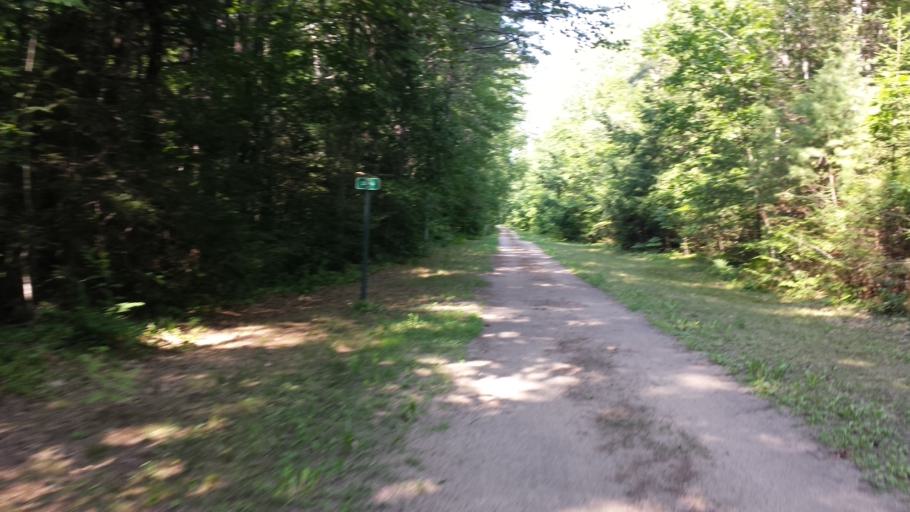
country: US
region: Maine
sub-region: York County
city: Kennebunk
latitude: 43.4384
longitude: -70.5261
